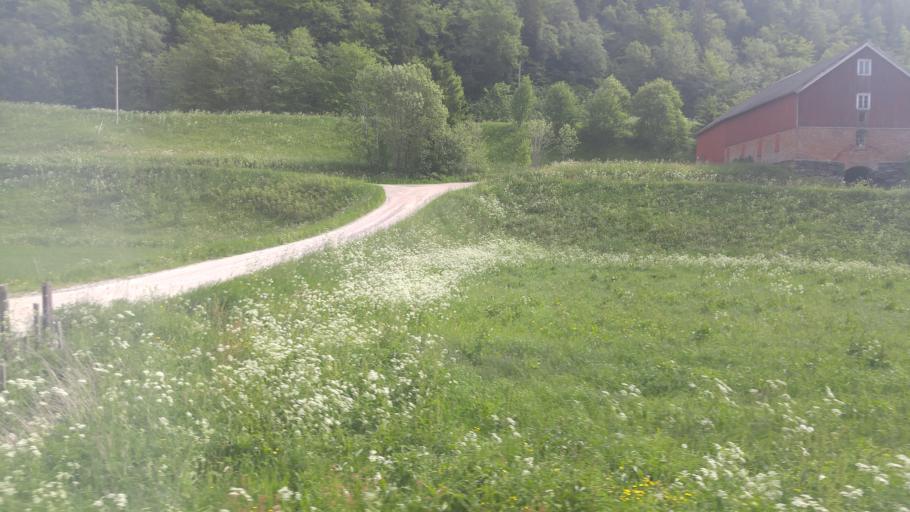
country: NO
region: Sor-Trondelag
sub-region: Midtre Gauldal
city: Storen
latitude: 63.0043
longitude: 10.4592
